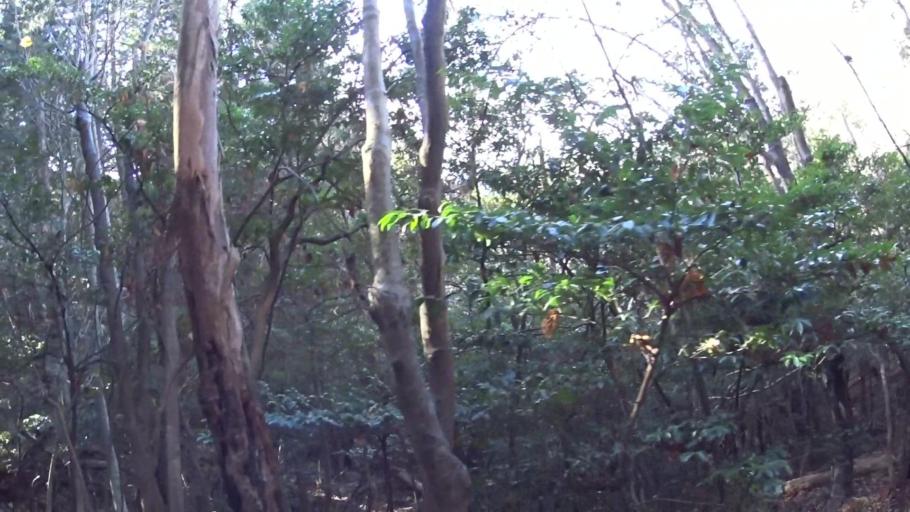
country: JP
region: Kyoto
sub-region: Kyoto-shi
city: Kamigyo-ku
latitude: 35.0973
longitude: 135.7579
